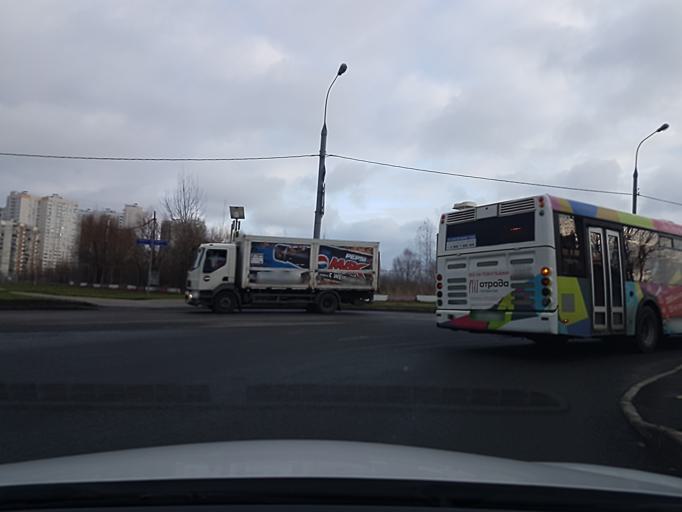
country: RU
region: Moskovskaya
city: Pavshino
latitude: 55.8402
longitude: 37.3505
